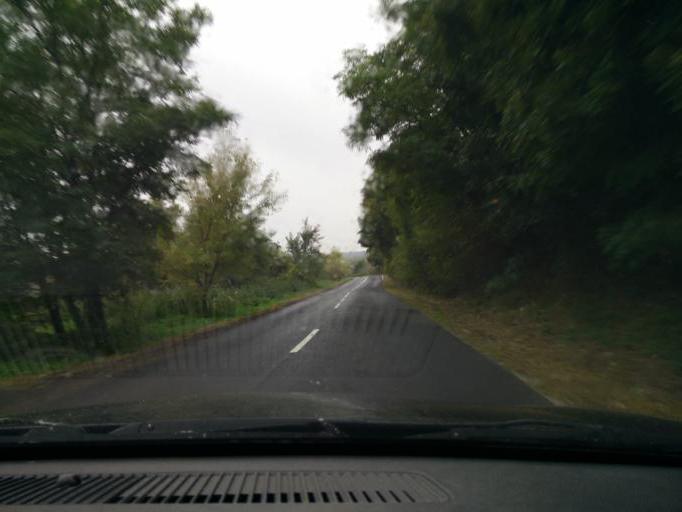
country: HU
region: Pest
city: Piliscsaba
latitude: 47.6441
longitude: 18.7829
